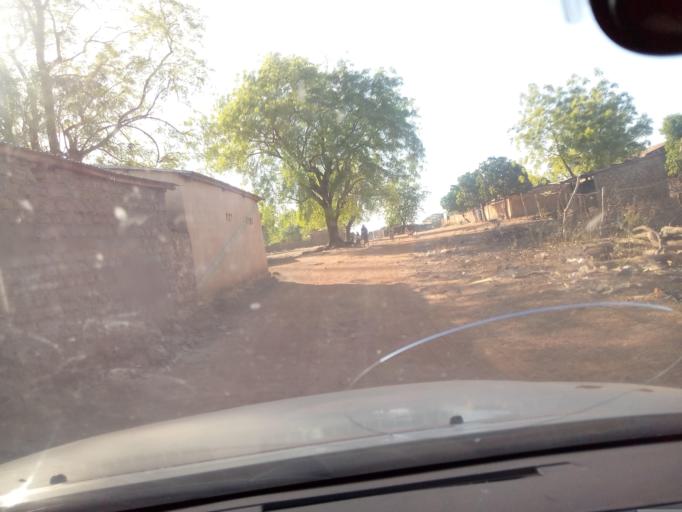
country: ML
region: Sikasso
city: Sikasso
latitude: 11.4861
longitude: -5.4815
